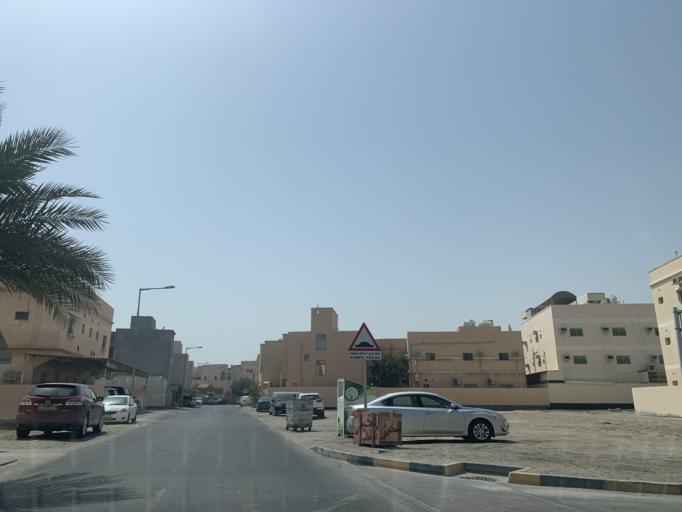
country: BH
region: Northern
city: Madinat `Isa
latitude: 26.1881
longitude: 50.5439
